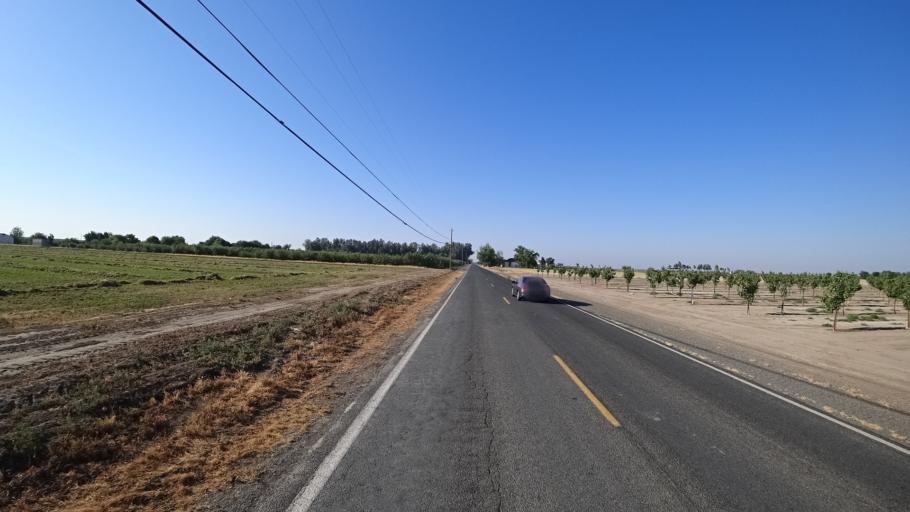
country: US
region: California
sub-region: Kings County
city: Armona
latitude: 36.2738
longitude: -119.7090
